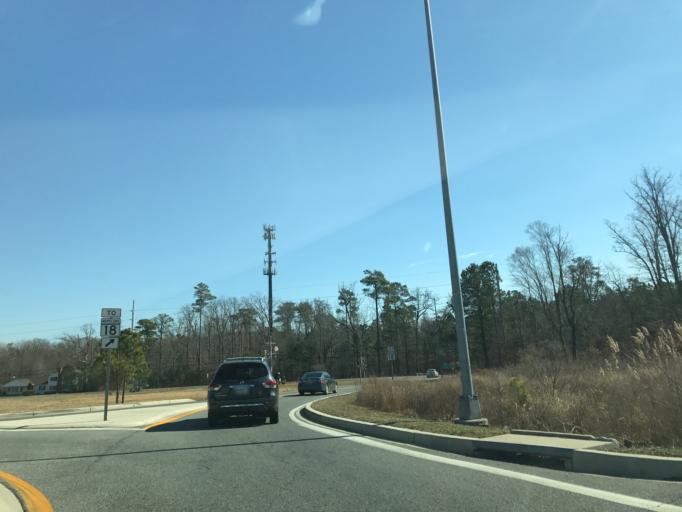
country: US
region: Maryland
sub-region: Queen Anne's County
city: Grasonville
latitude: 38.9659
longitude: -76.1830
